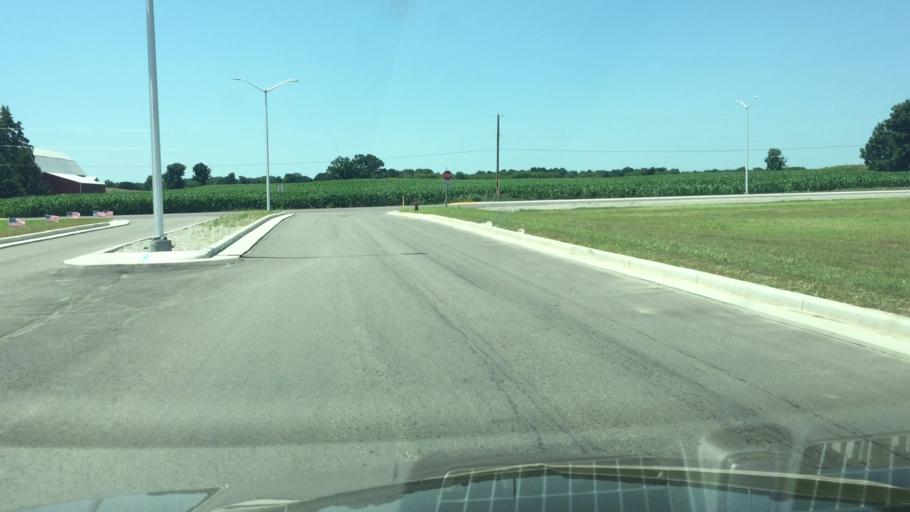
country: US
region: Wisconsin
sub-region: Fond du Lac County
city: Waupun
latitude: 43.6080
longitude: -88.7238
